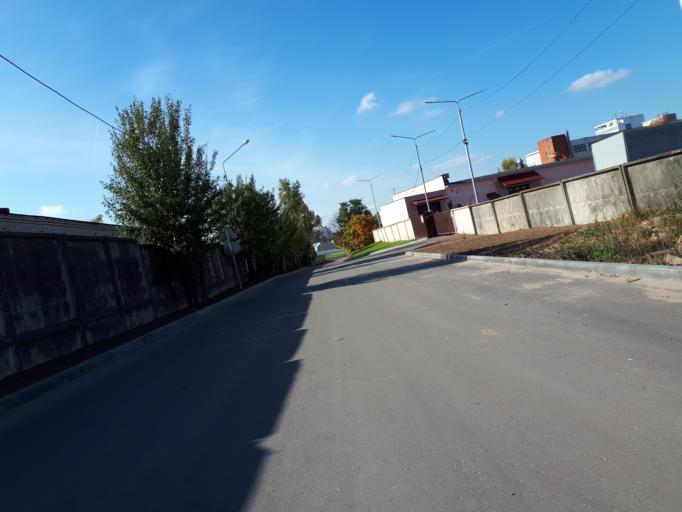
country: BY
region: Vitebsk
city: Vitebsk
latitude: 55.1639
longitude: 30.2436
